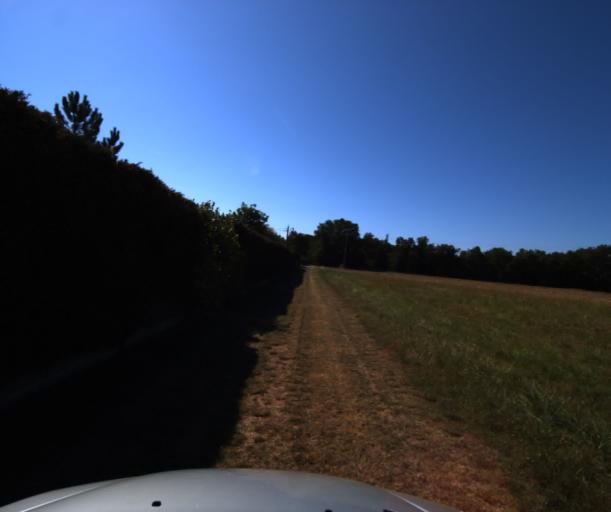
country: FR
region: Midi-Pyrenees
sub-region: Departement de la Haute-Garonne
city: Eaunes
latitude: 43.4117
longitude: 1.3596
